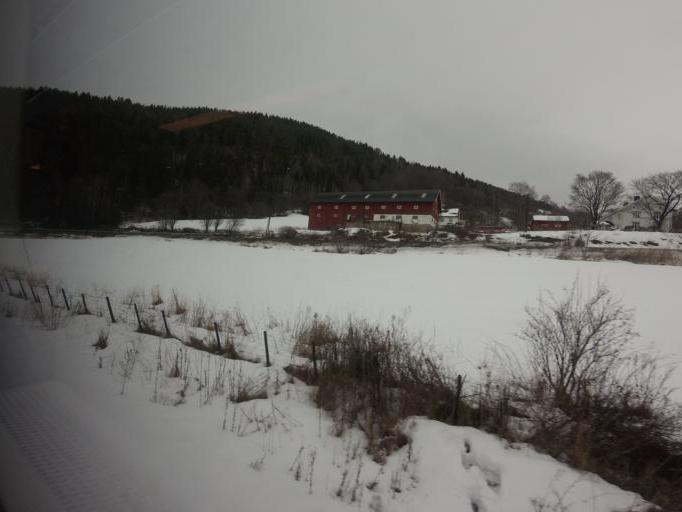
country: NO
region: Hedmark
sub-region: Ringsaker
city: Moelv
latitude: 60.9621
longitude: 10.6648
